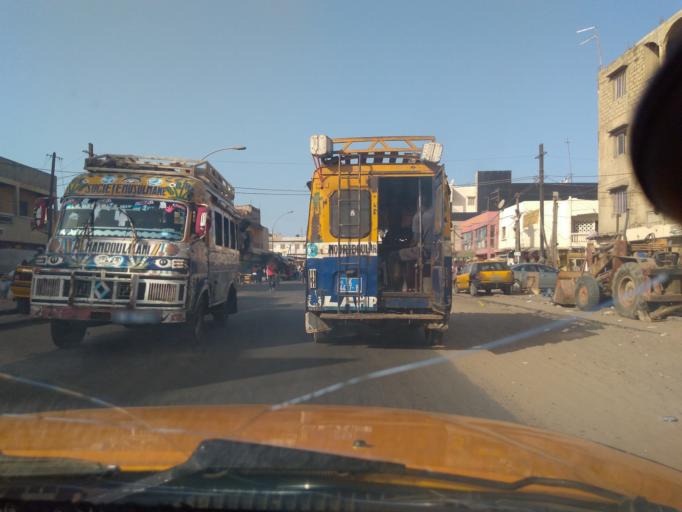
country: SN
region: Dakar
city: Grand Dakar
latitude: 14.7403
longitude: -17.4466
